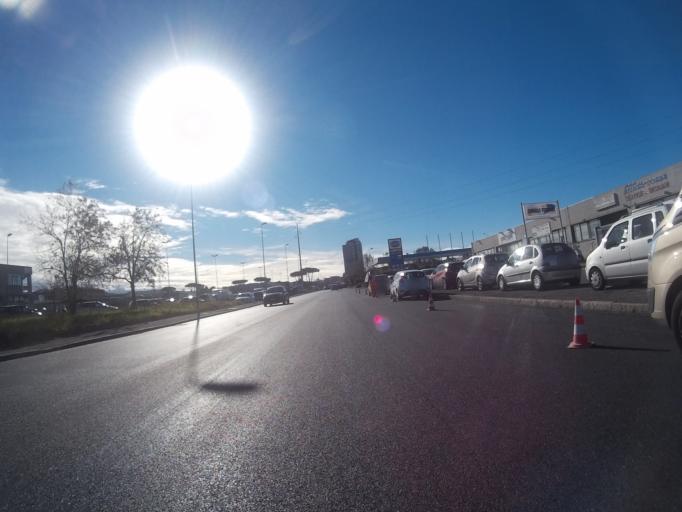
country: IT
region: Tuscany
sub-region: Provincia di Livorno
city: Livorno
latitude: 43.5661
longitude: 10.3421
